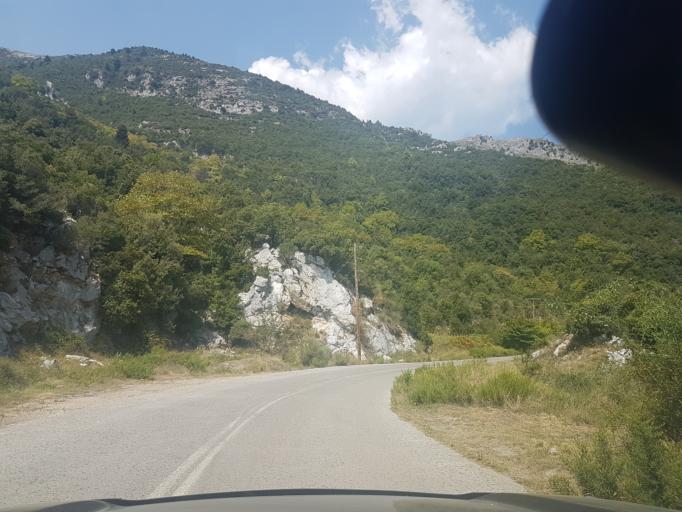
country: GR
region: Central Greece
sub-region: Nomos Evvoias
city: Yimnon
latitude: 38.6331
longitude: 23.8912
